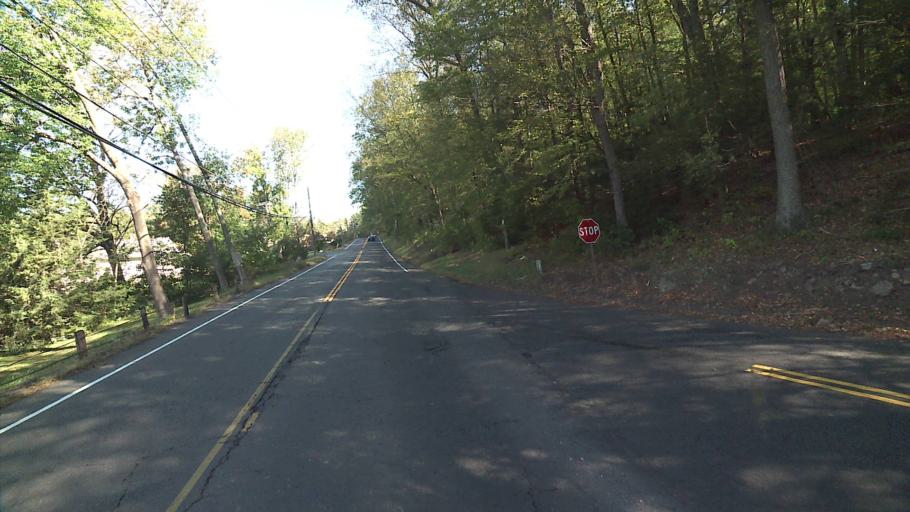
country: US
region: Connecticut
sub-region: Tolland County
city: Ellington
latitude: 41.9375
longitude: -72.4524
